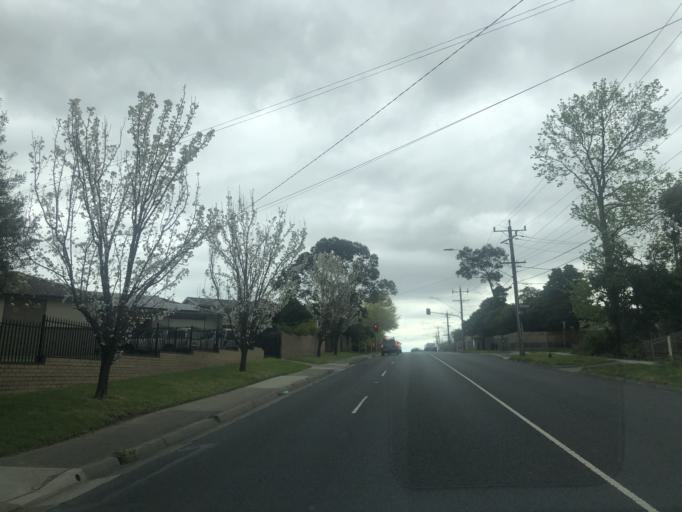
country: AU
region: Victoria
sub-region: Casey
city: Doveton
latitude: -37.9860
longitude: 145.2243
